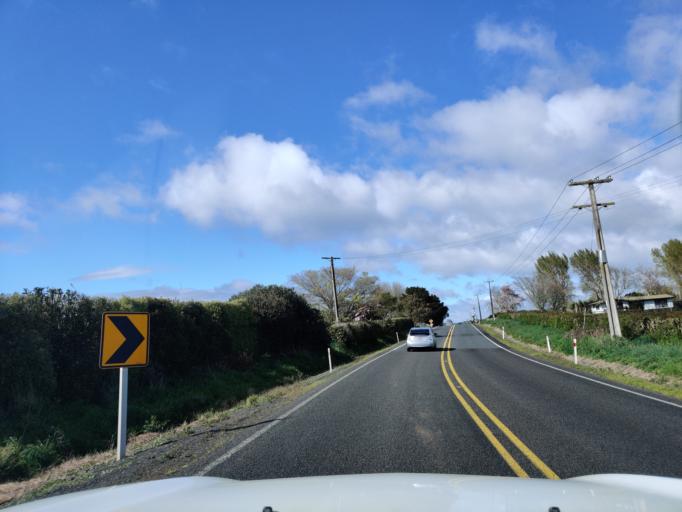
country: NZ
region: Waikato
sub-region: Otorohanga District
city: Otorohanga
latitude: -38.0996
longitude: 175.1894
